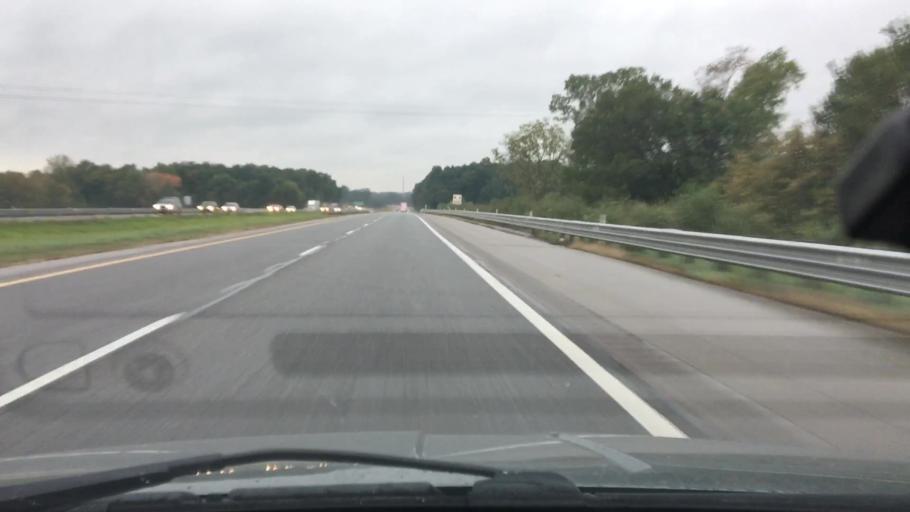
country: US
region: Michigan
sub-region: Washtenaw County
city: Dexter
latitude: 42.2980
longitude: -83.9351
